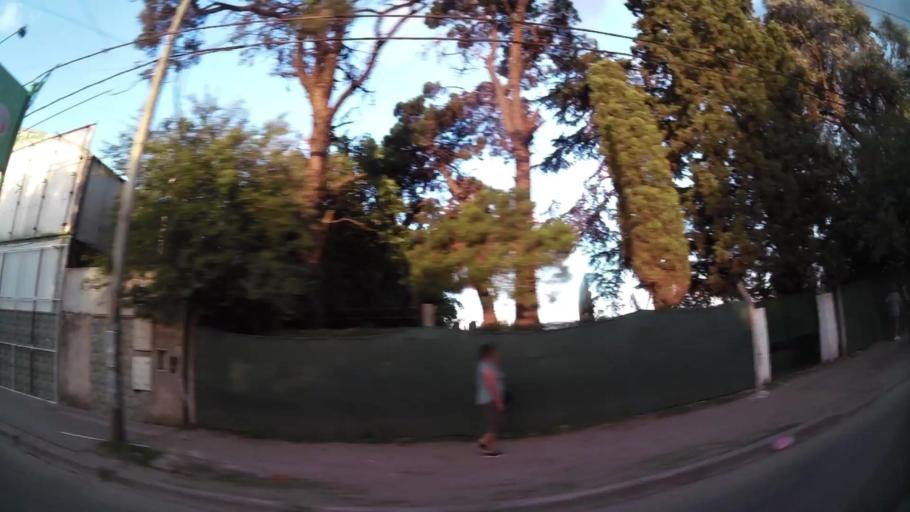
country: AR
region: Buenos Aires
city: Santa Catalina - Dique Lujan
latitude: -34.4836
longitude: -58.7510
